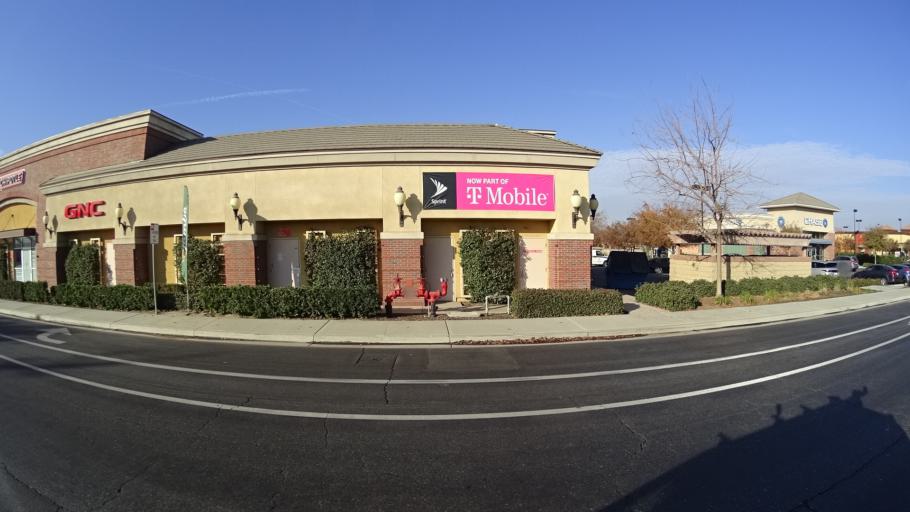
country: US
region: California
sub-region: Kern County
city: Greenacres
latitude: 35.3068
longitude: -119.0923
